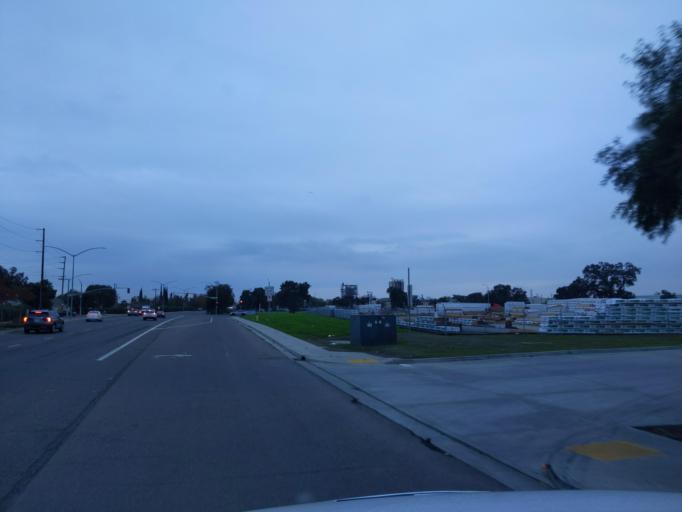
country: US
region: California
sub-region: San Joaquin County
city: Kennedy
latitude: 37.9213
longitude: -121.2631
